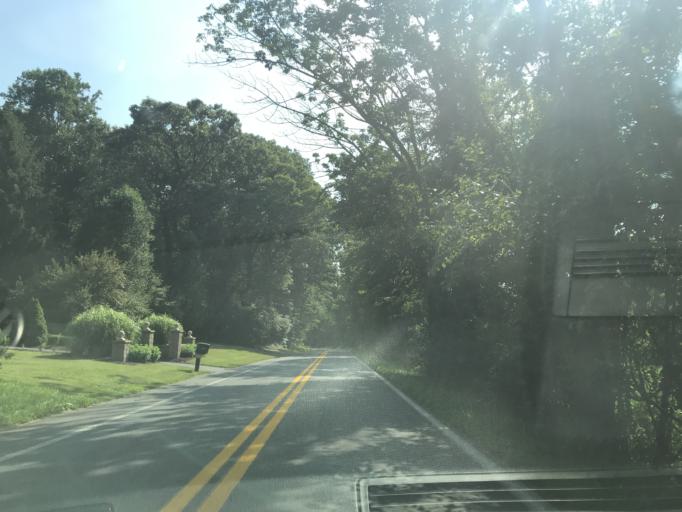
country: US
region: Maryland
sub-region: Carroll County
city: Manchester
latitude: 39.6716
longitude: -76.8982
